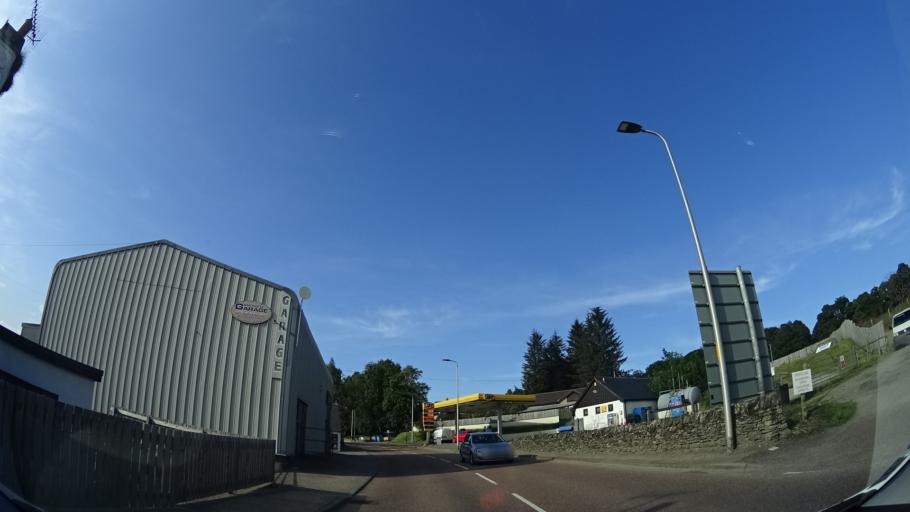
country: GB
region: Scotland
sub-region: Highland
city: Muir of Ord
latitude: 57.5671
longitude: -4.5791
